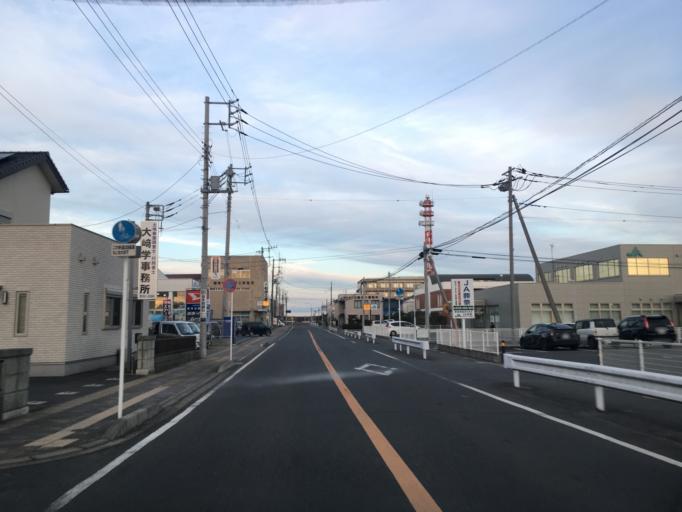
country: JP
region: Chiba
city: Katori-shi
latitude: 35.8980
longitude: 140.5006
